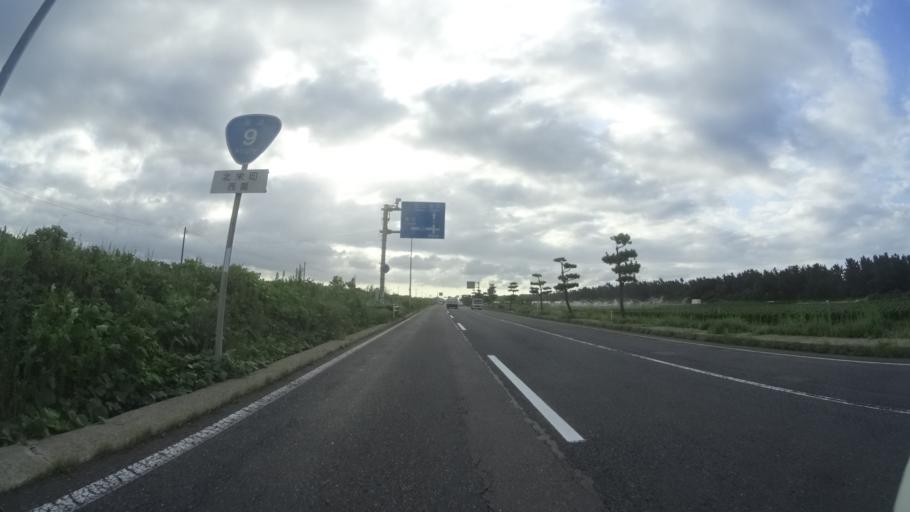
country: JP
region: Tottori
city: Kurayoshi
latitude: 35.4983
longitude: 133.7777
